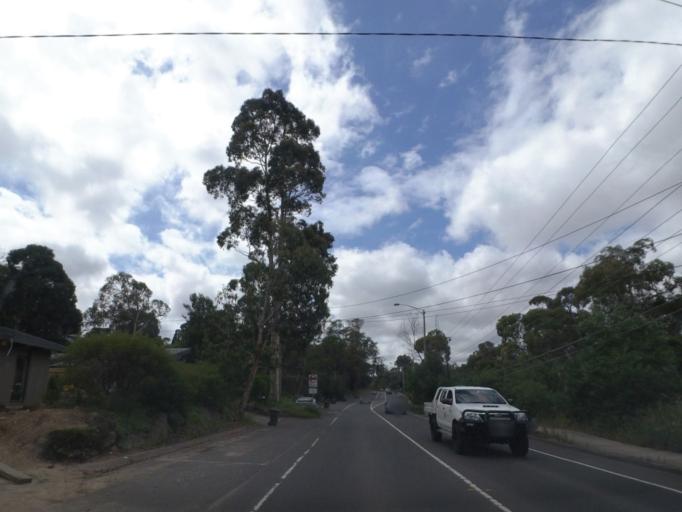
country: AU
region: Victoria
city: Saint Helena
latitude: -37.7122
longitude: 145.1333
